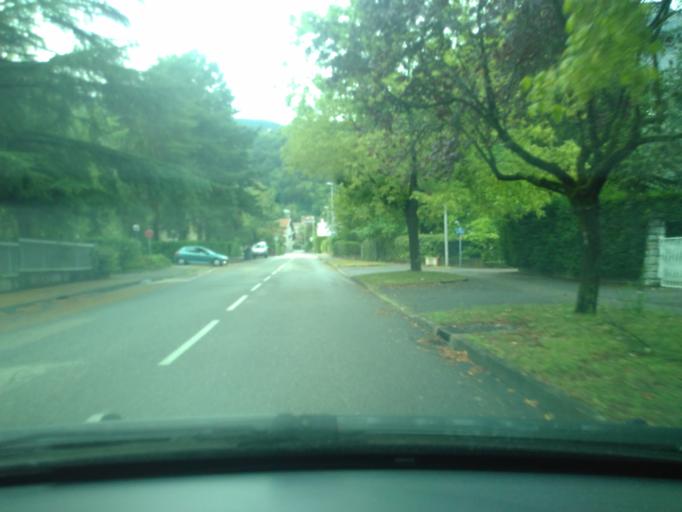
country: FR
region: Rhone-Alpes
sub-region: Departement de l'Isere
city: Corenc
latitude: 45.2104
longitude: 5.7672
